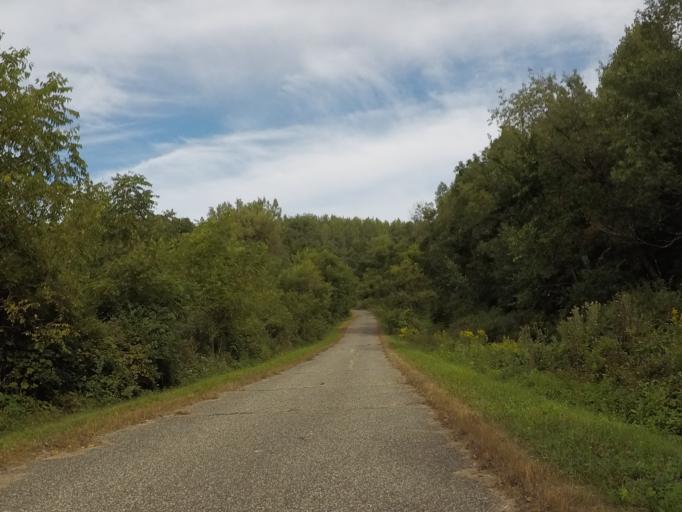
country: US
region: Wisconsin
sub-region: Sauk County
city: Baraboo
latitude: 43.3833
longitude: -89.7199
